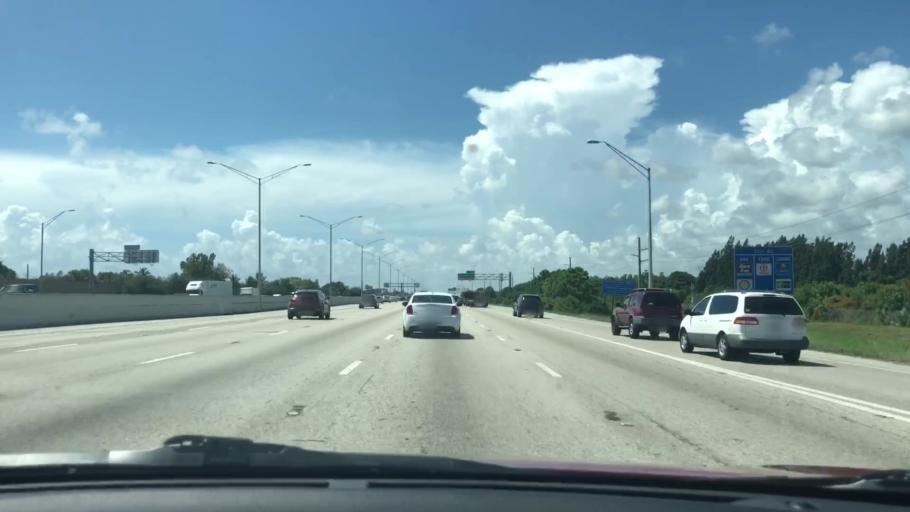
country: US
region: Florida
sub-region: Palm Beach County
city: Lantana
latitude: 26.5833
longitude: -80.0695
